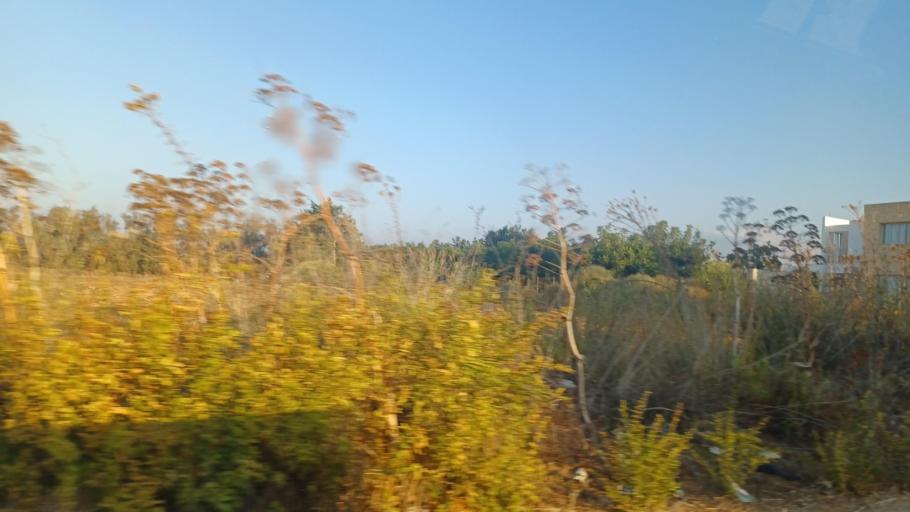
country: CY
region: Pafos
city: Empa
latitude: 34.8030
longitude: 32.4364
